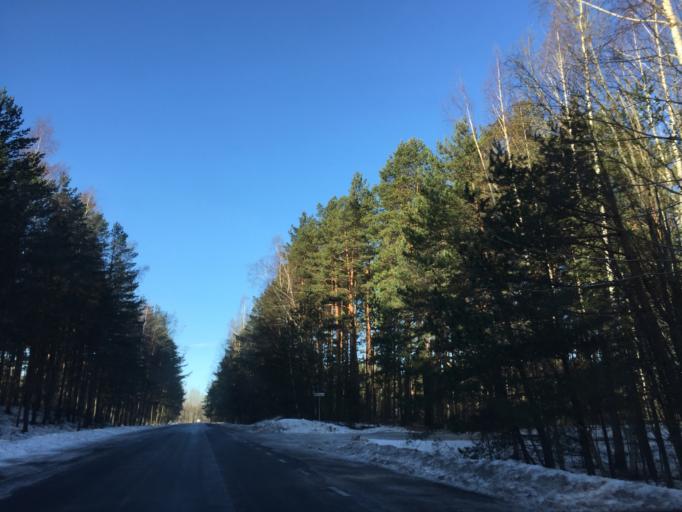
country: LV
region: Salacgrivas
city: Ainazi
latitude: 58.0761
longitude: 24.5021
